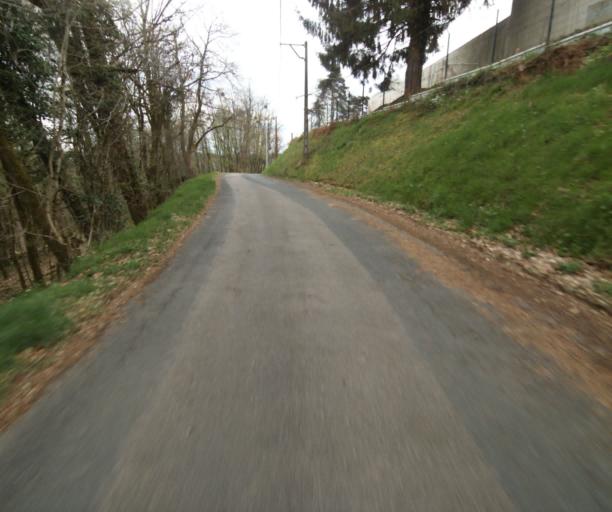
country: FR
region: Limousin
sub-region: Departement de la Correze
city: Tulle
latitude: 45.2548
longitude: 1.7693
